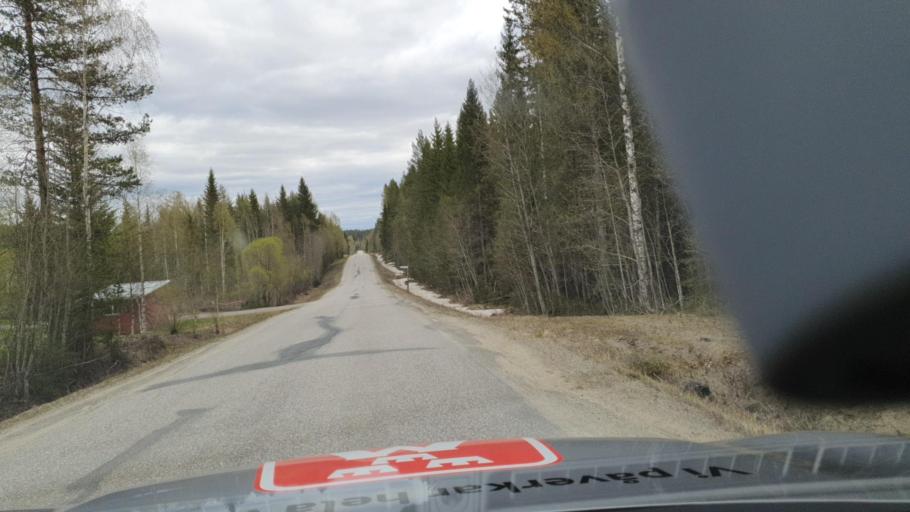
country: SE
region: Vaesternorrland
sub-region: OErnskoeldsviks Kommun
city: Ornskoldsvik
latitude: 63.6880
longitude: 18.8128
